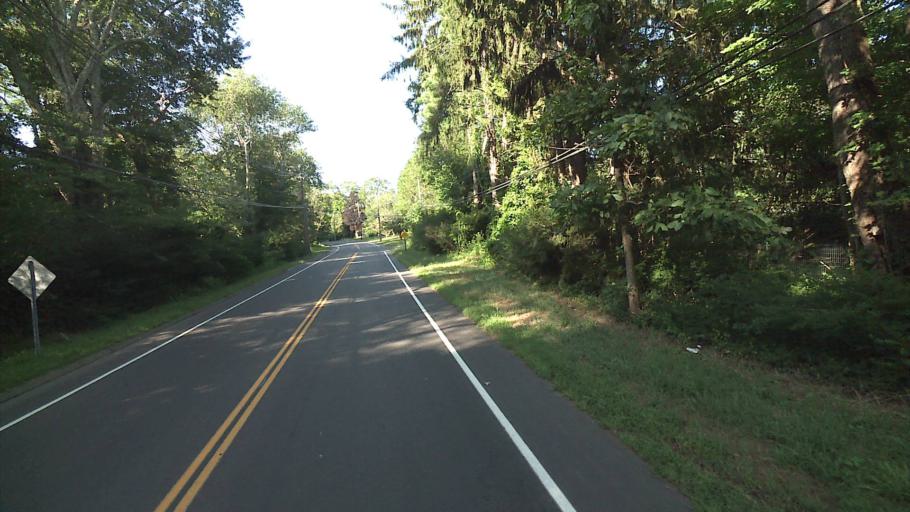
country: US
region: Connecticut
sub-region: Middlesex County
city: Old Saybrook Center
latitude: 41.3303
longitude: -72.3235
